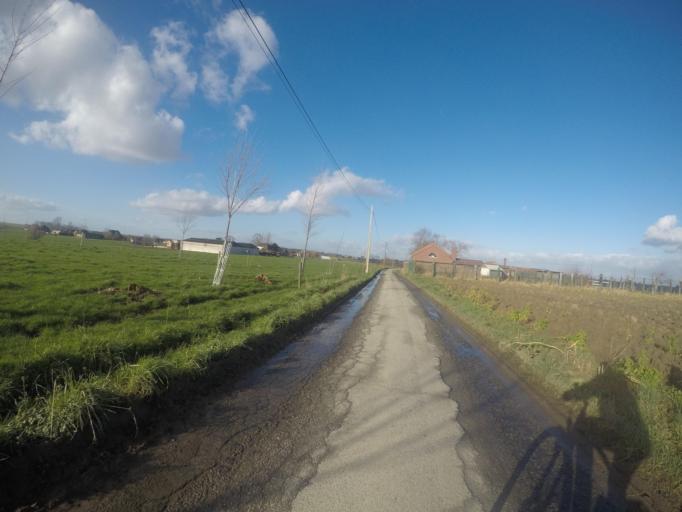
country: BE
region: Wallonia
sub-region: Province du Brabant Wallon
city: Rebecq-Rognon
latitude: 50.6579
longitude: 4.1221
